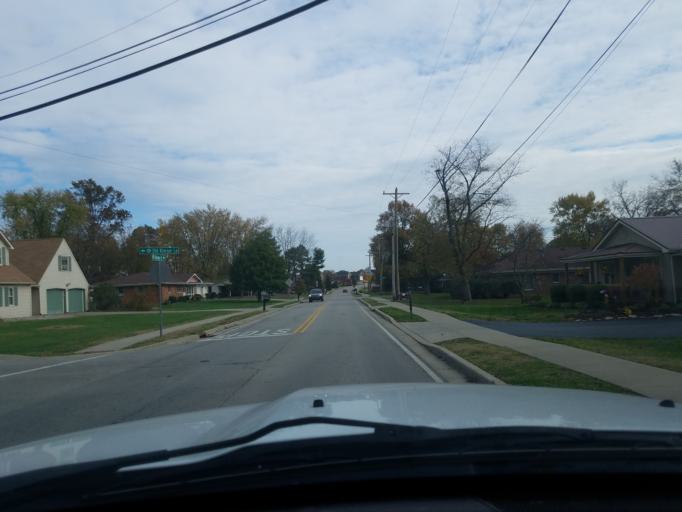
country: US
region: Indiana
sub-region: Floyd County
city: New Albany
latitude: 38.3370
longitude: -85.8089
